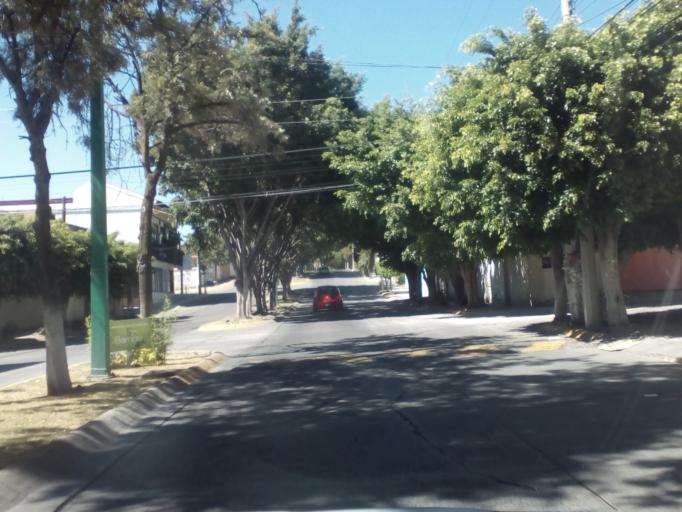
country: MX
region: Guanajuato
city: Leon
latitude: 21.1204
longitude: -101.7026
